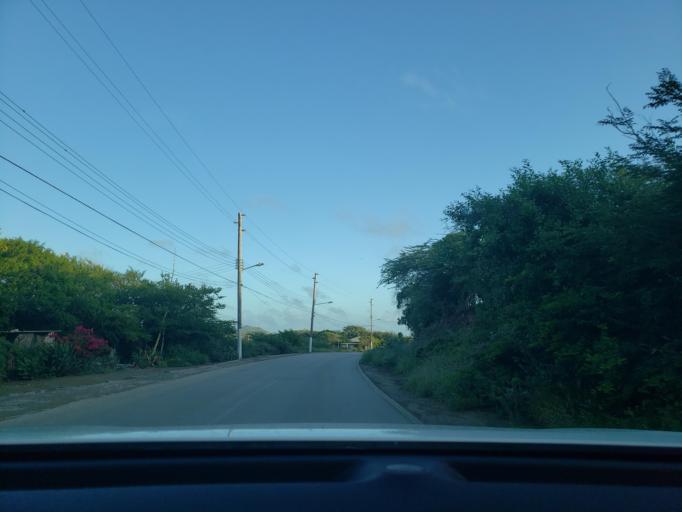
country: CW
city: Barber
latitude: 12.2615
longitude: -69.0681
